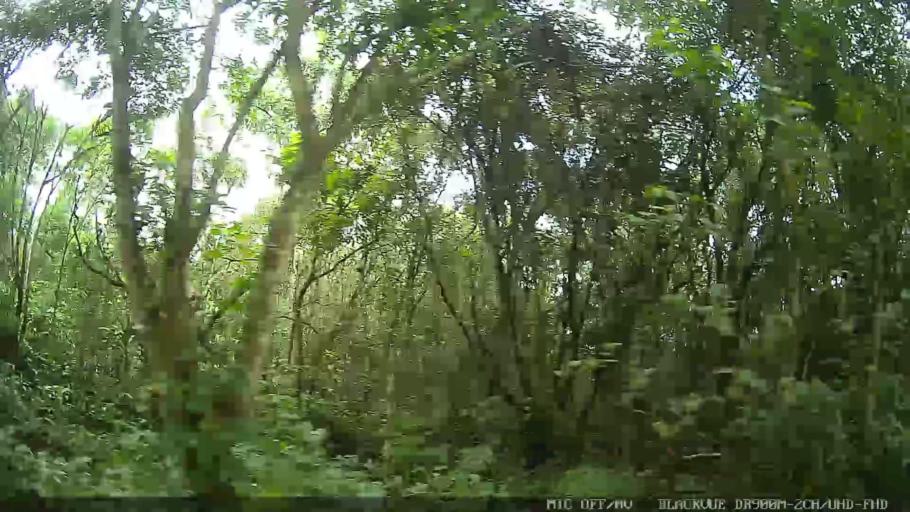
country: BR
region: Sao Paulo
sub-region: Itanhaem
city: Itanhaem
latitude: -24.2140
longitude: -46.8860
